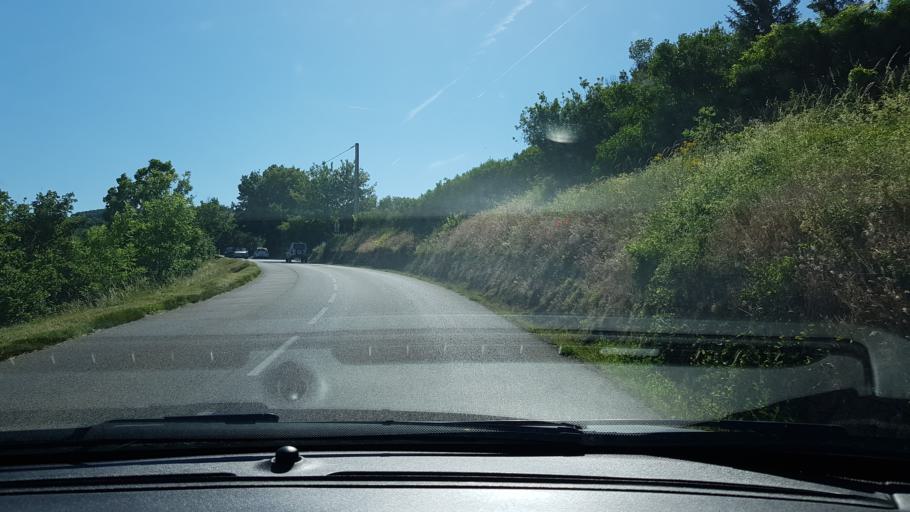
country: FR
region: Rhone-Alpes
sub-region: Departement du Rhone
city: Saint-Didier-sous-Riverie
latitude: 45.5960
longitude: 4.5945
